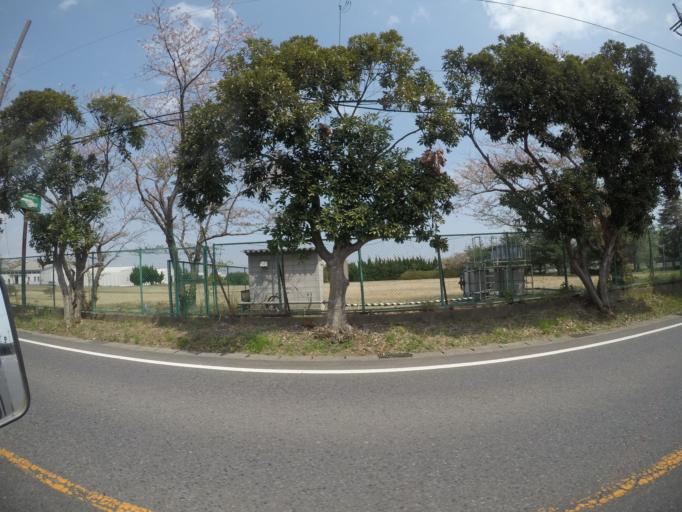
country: JP
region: Chiba
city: Omigawa
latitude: 35.8579
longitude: 140.5564
